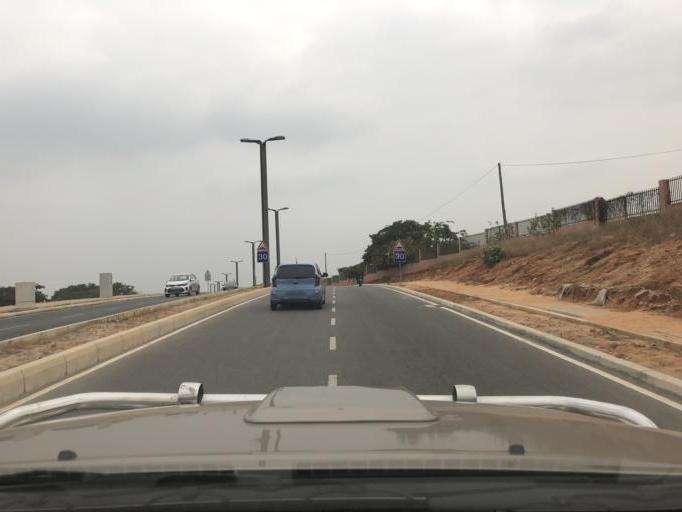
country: AO
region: Luanda
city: Luanda
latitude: -8.8975
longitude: 13.1753
